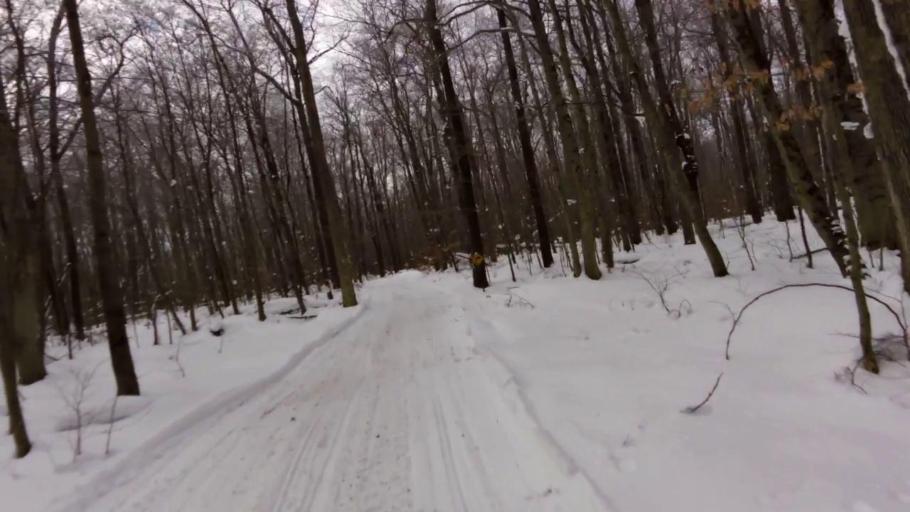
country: US
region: Pennsylvania
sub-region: McKean County
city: Bradford
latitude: 42.0260
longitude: -78.7401
